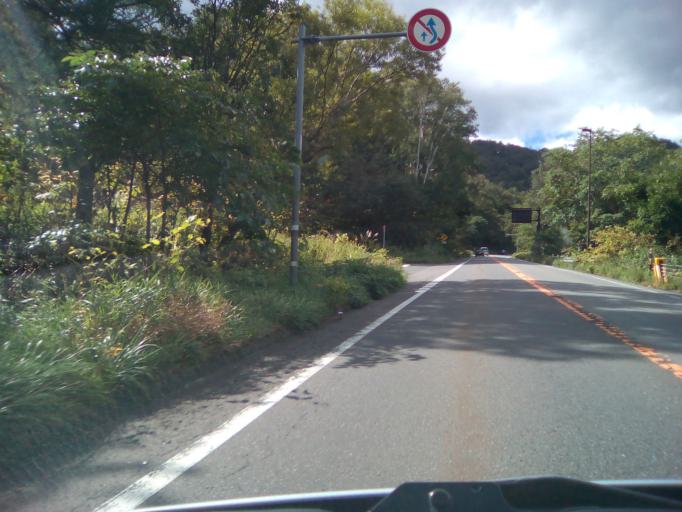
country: JP
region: Hokkaido
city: Date
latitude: 42.5907
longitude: 140.7854
